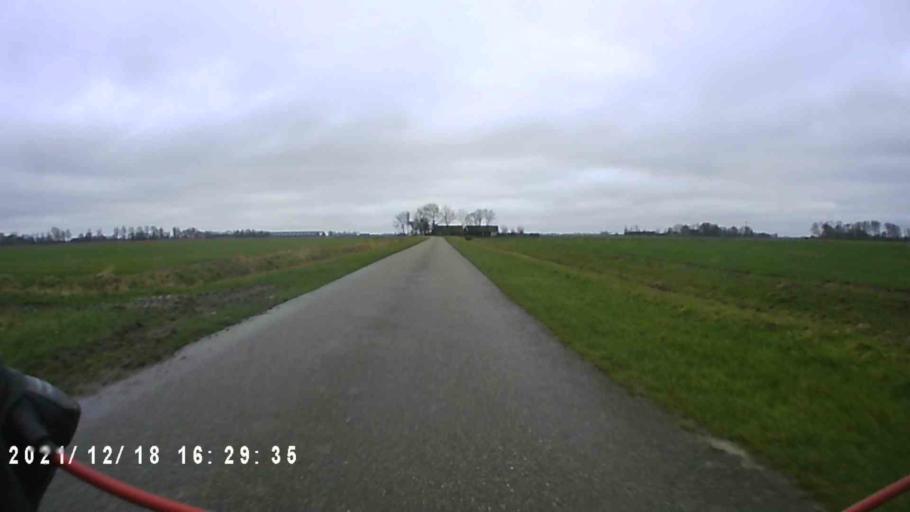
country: NL
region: Friesland
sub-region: Gemeente Dongeradeel
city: Dokkum
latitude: 53.3627
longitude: 6.0357
